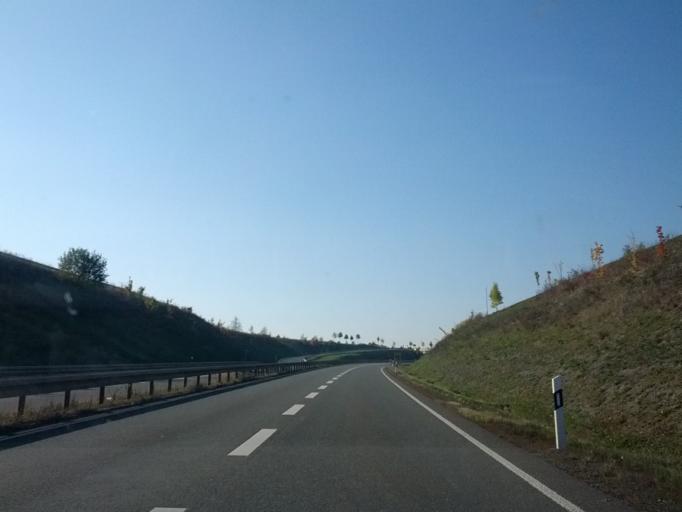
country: DE
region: Thuringia
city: Schwaara
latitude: 50.9000
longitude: 12.1234
